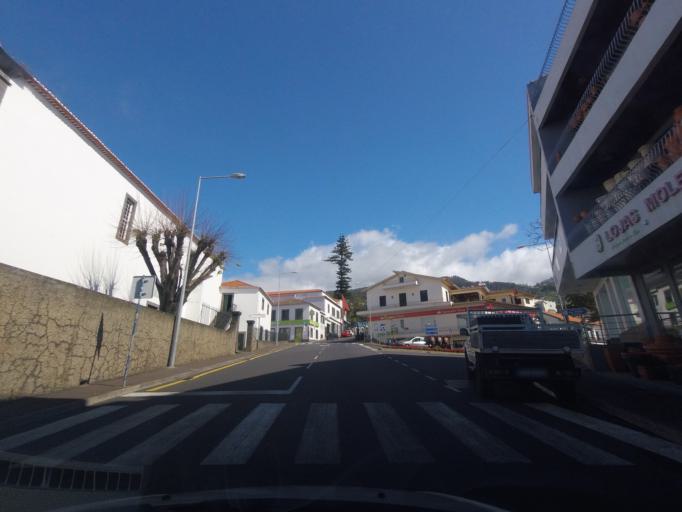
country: PT
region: Madeira
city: Camara de Lobos
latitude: 32.6711
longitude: -16.9798
